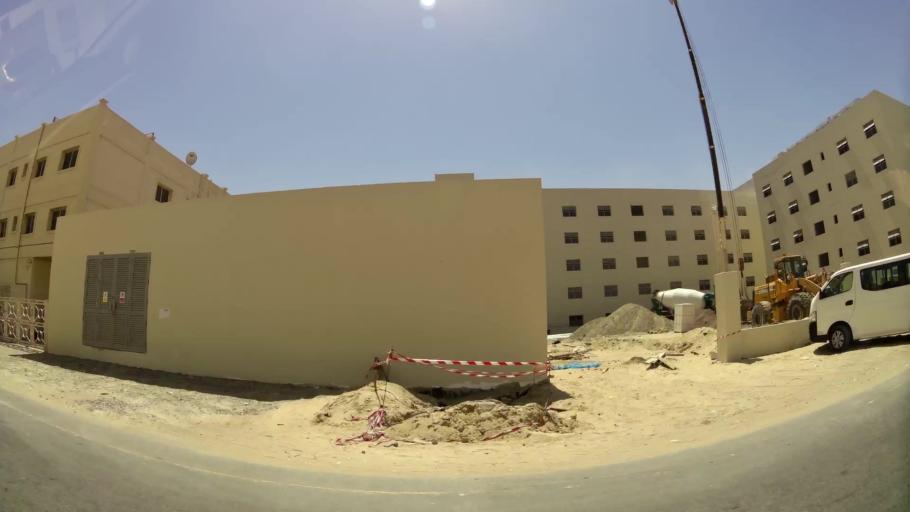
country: AE
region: Dubai
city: Dubai
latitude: 24.9893
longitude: 55.1970
